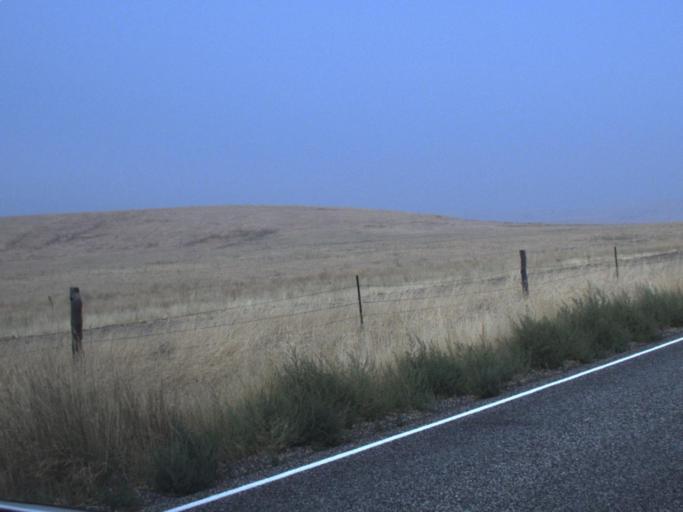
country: US
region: Washington
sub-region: Yakima County
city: Sunnyside
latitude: 46.4059
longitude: -119.9493
